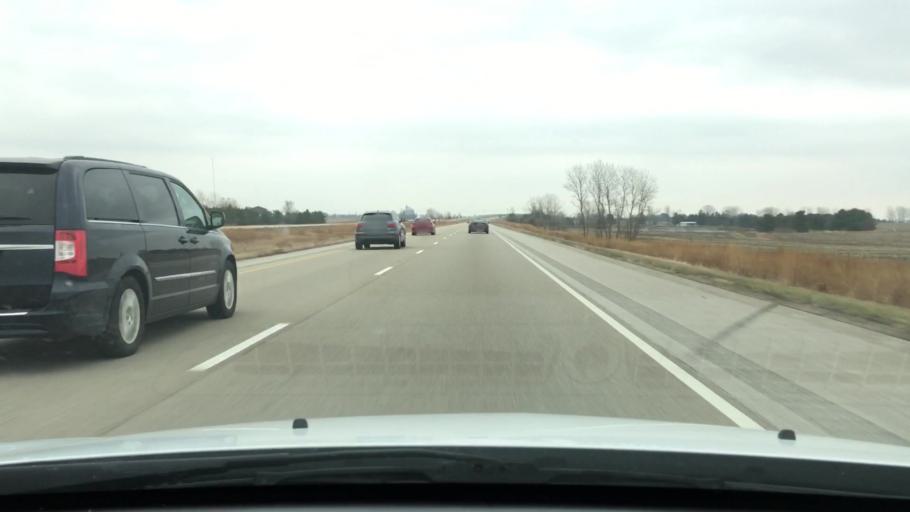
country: US
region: Illinois
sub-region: Logan County
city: Lincoln
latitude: 40.1829
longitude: -89.3391
